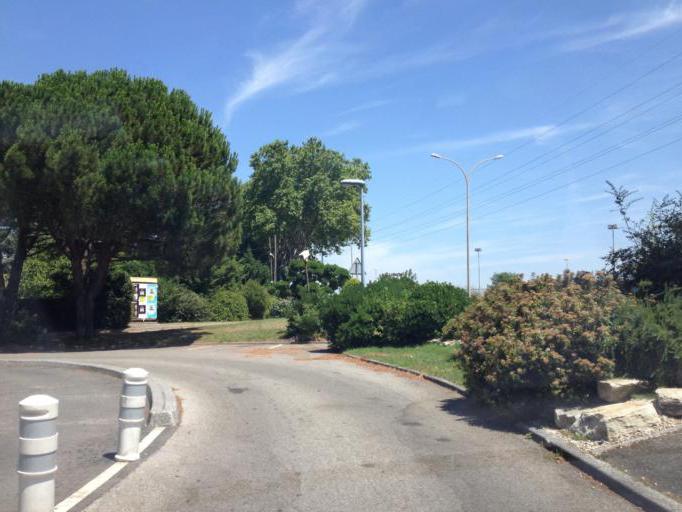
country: FR
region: Rhone-Alpes
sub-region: Departement de la Drome
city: Bourg-les-Valence
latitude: 44.9406
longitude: 4.9158
